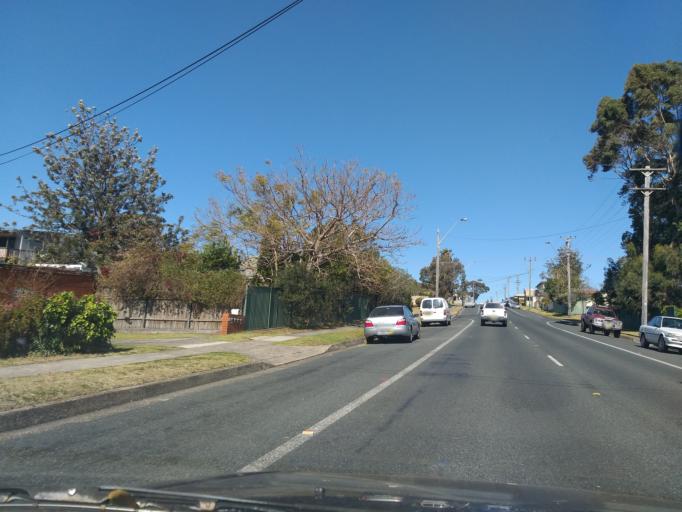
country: AU
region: New South Wales
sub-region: Wollongong
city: East Corrimal
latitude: -34.3653
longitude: 150.9109
